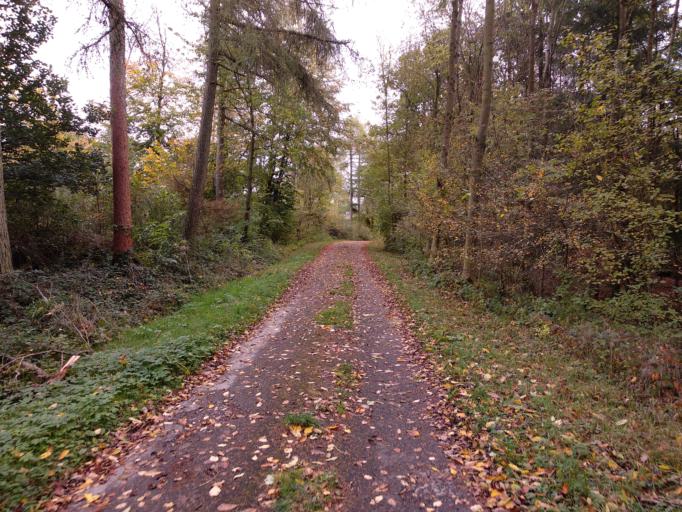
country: DE
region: North Rhine-Westphalia
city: Beverungen
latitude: 51.6697
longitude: 9.3406
